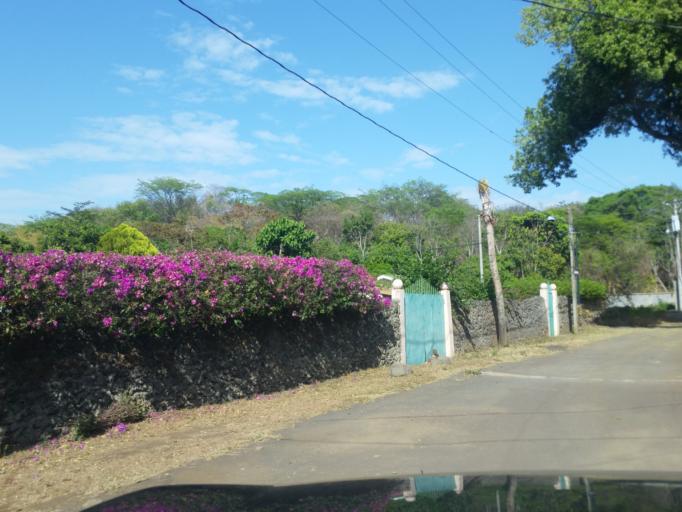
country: NI
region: Masaya
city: Ticuantepe
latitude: 12.0288
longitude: -86.1769
